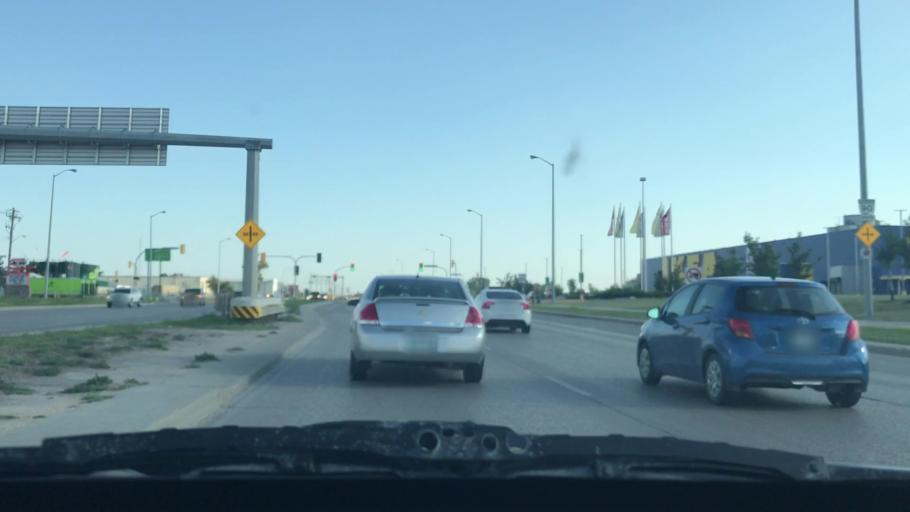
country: CA
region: Manitoba
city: Winnipeg
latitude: 49.8408
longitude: -97.2090
